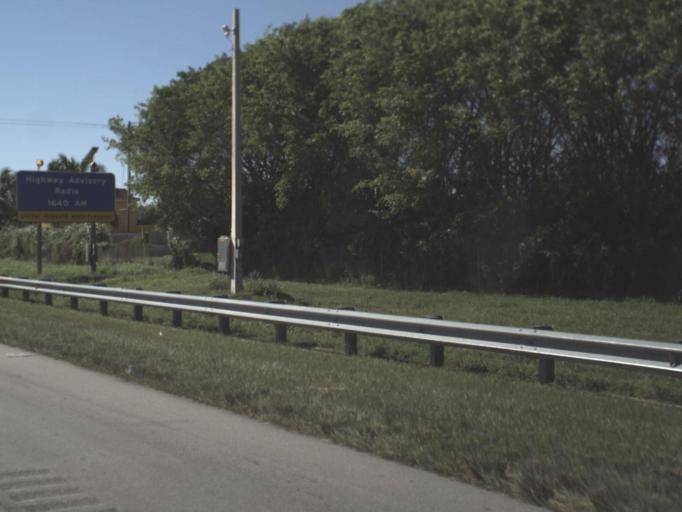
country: US
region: Florida
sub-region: Miami-Dade County
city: Goulds
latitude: 25.5450
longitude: -80.3630
